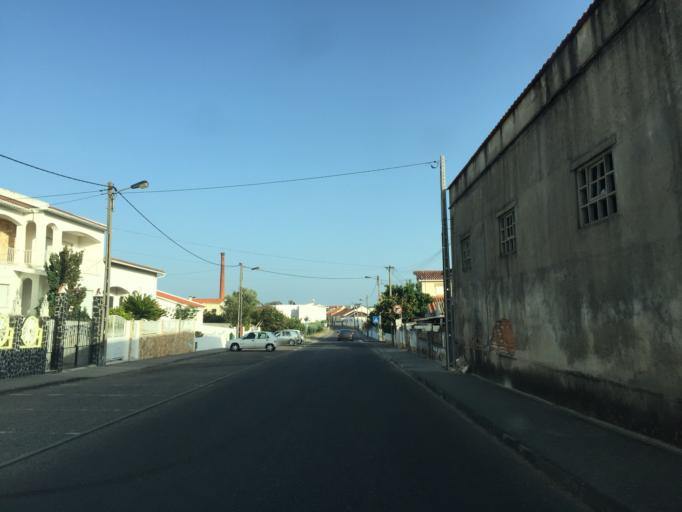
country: PT
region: Santarem
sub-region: Chamusca
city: Vila Nova da Barquinha
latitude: 39.4690
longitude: -8.4415
